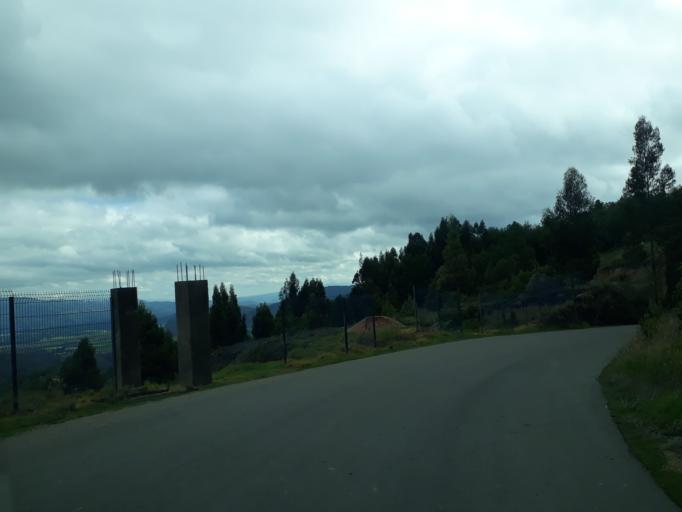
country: CO
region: Cundinamarca
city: Cucunuba
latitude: 5.2166
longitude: -73.7831
